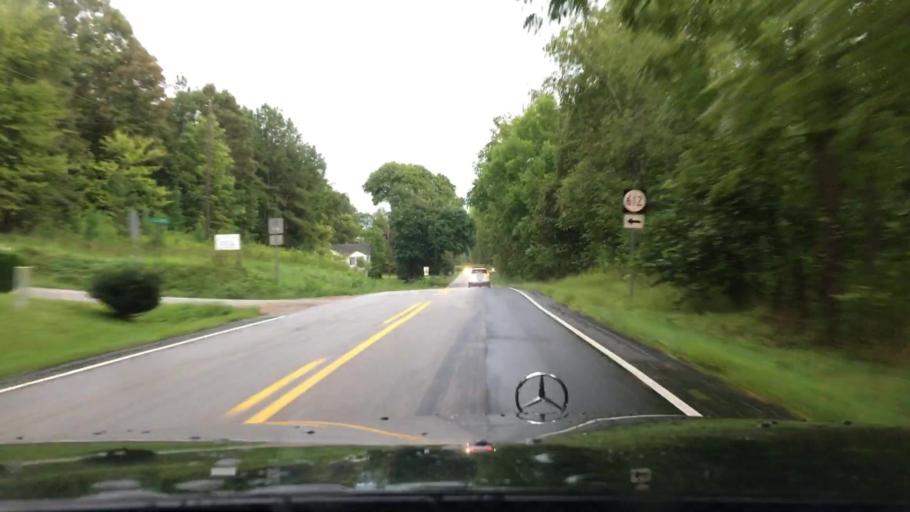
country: US
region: Virginia
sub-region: Amherst County
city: Amherst
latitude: 37.6676
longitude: -79.0121
